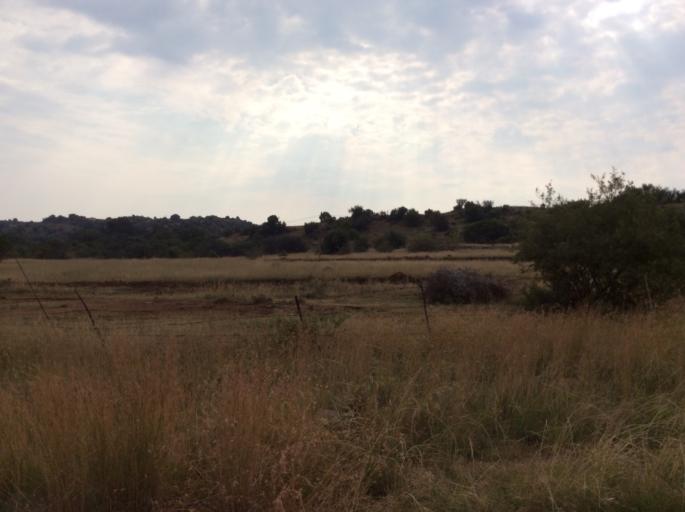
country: LS
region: Mafeteng
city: Mafeteng
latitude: -29.9861
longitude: 27.0189
